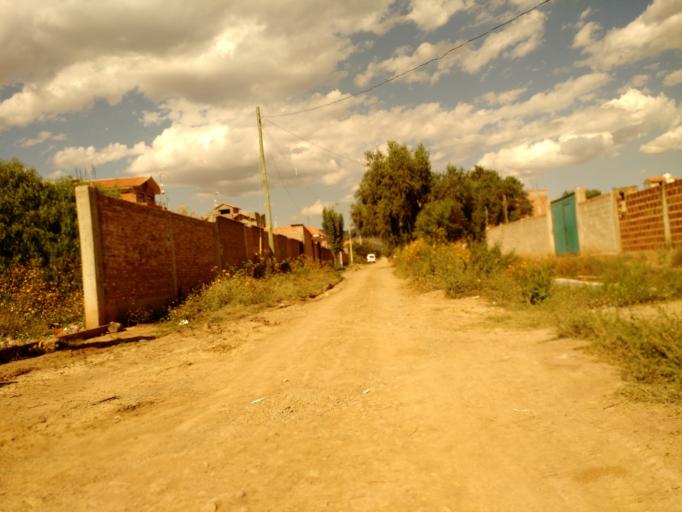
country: BO
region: Cochabamba
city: Cochabamba
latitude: -17.4586
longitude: -66.1539
